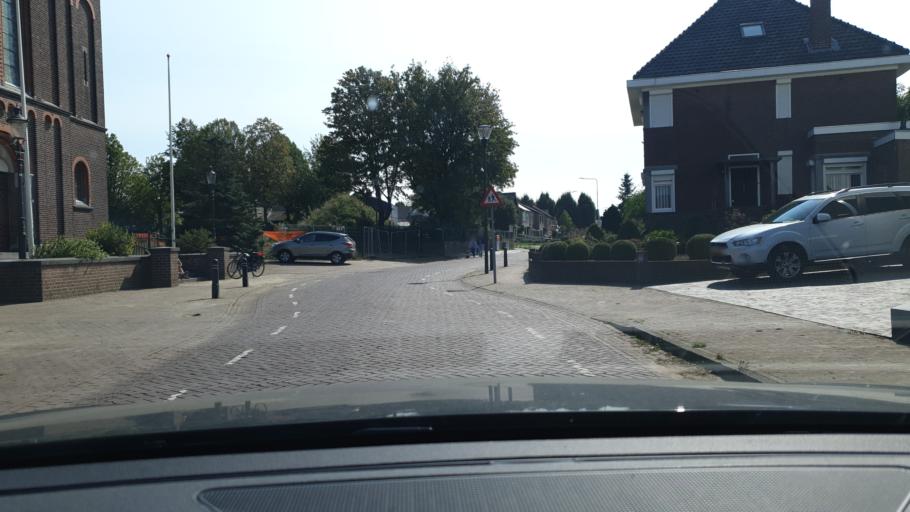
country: NL
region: Limburg
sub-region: Gemeente Sittard-Geleen
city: Limbricht
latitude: 51.0019
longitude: 5.8265
